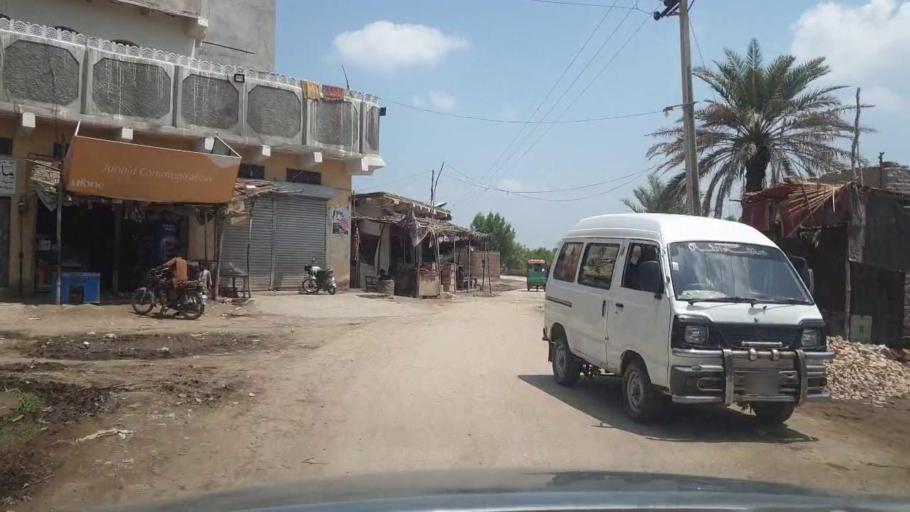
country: PK
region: Sindh
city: Pir jo Goth
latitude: 27.5985
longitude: 68.6060
